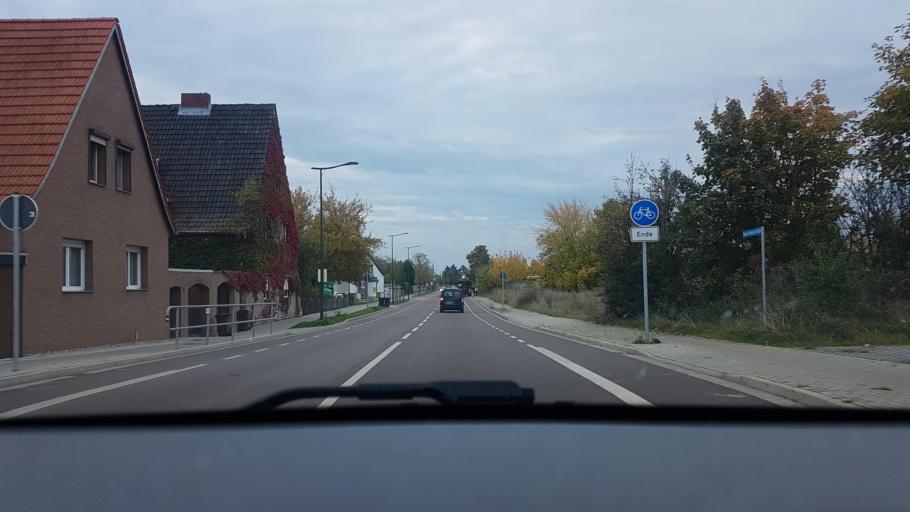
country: DE
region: Saxony-Anhalt
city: Bernburg
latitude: 51.7859
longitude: 11.7580
